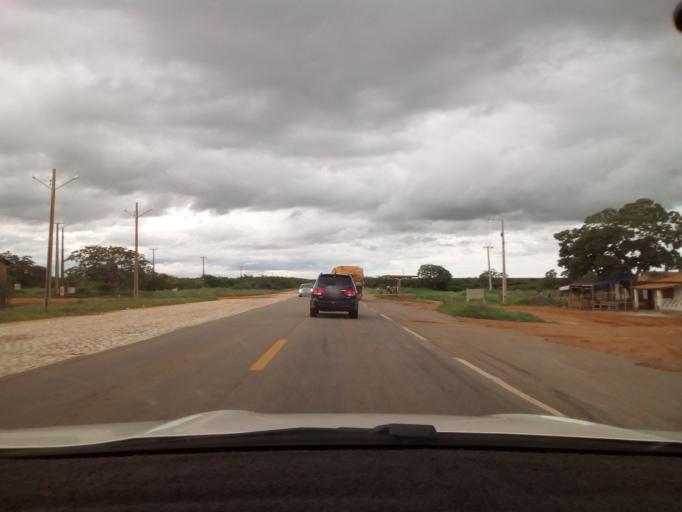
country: BR
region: Rio Grande do Norte
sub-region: Barauna
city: Barauna
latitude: -4.9252
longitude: -37.4184
